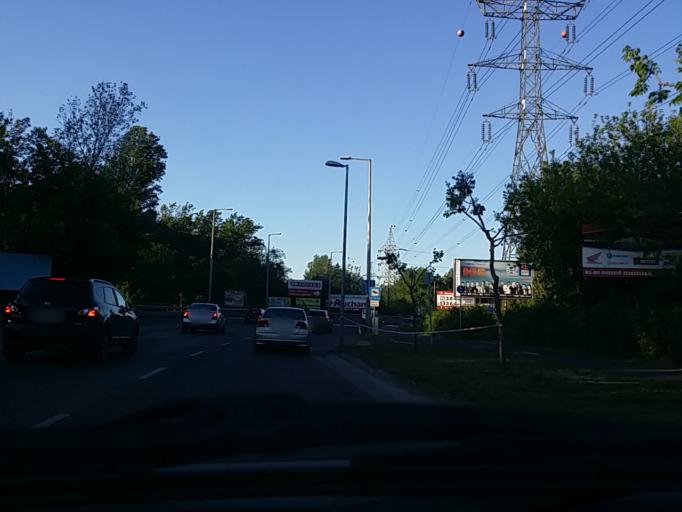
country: HU
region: Budapest
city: Budapest IV. keruelet
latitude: 47.5946
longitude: 19.0888
